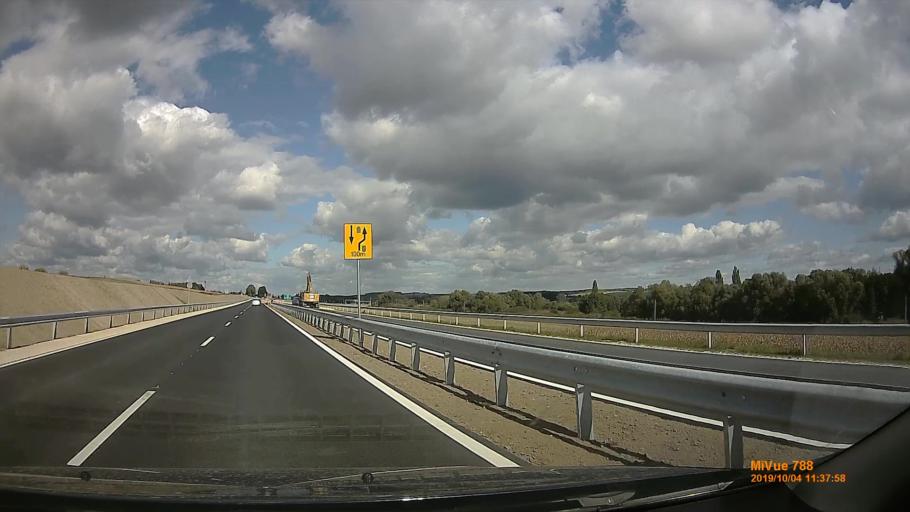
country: HU
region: Somogy
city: Karad
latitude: 46.5425
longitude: 17.8153
